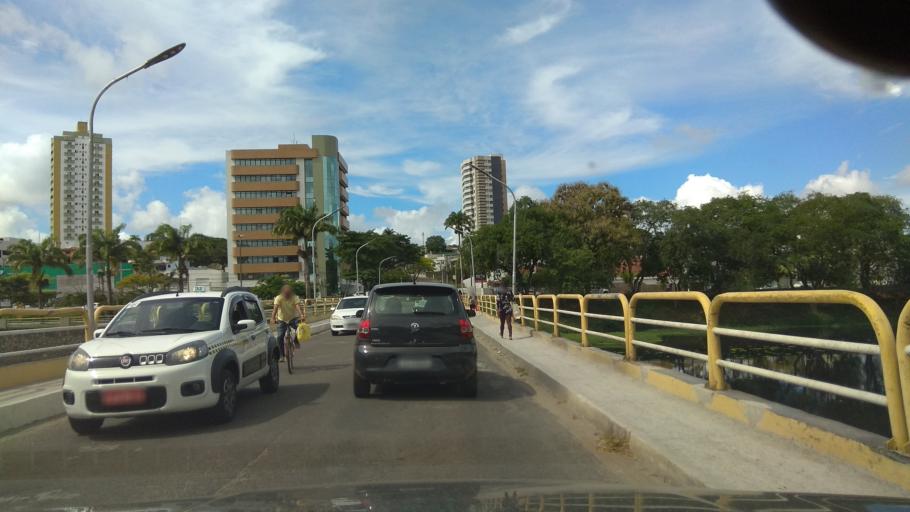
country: BR
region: Bahia
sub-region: Itabuna
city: Itabuna
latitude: -14.7931
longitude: -39.2744
